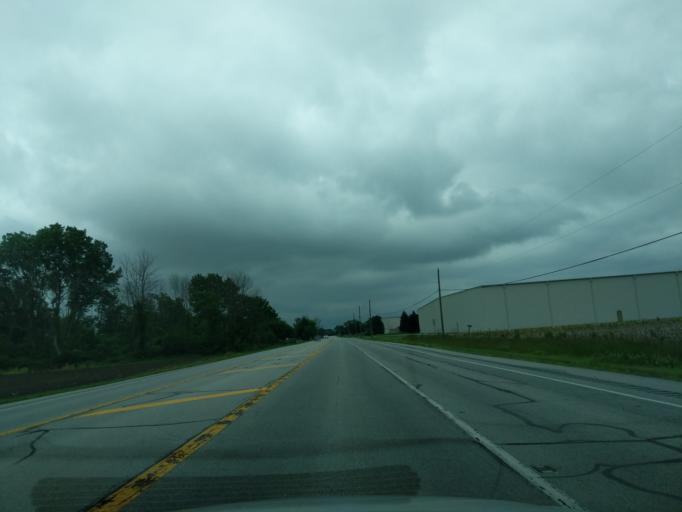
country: US
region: Indiana
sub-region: Madison County
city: Alexandria
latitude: 40.2774
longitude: -85.7246
